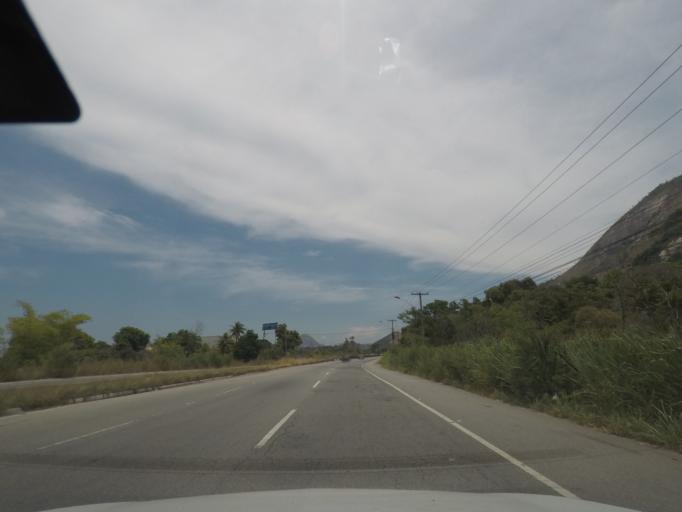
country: BR
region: Rio de Janeiro
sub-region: Marica
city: Marica
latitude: -22.9355
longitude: -42.9074
